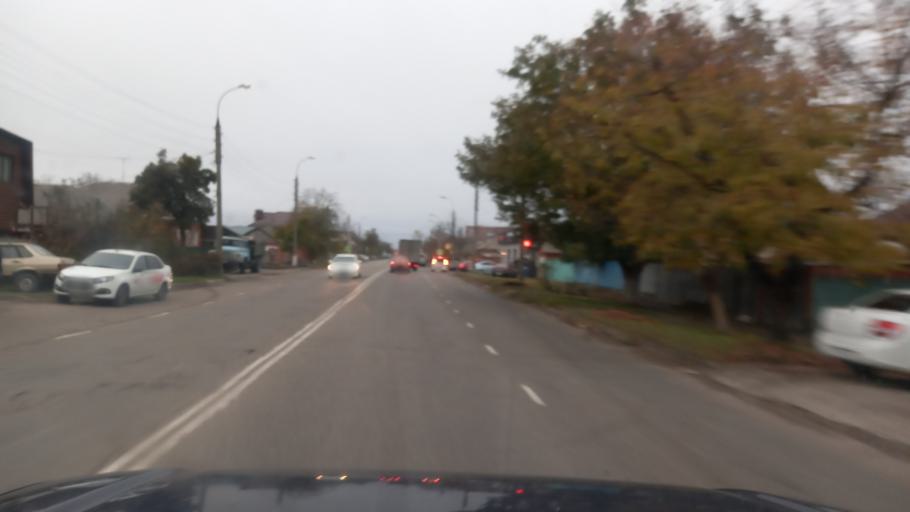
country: RU
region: Adygeya
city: Maykop
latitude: 44.6209
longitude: 40.0759
